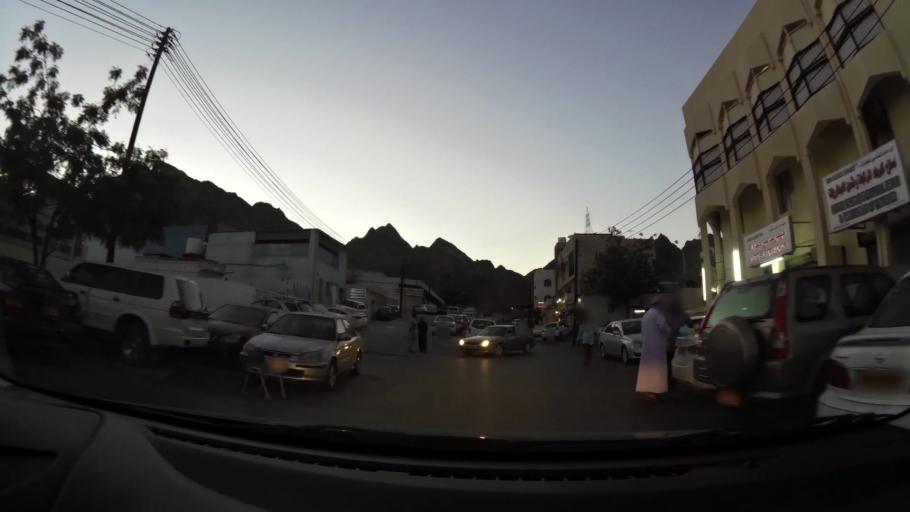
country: OM
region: Muhafazat Masqat
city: Muscat
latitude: 23.5951
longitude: 58.5604
